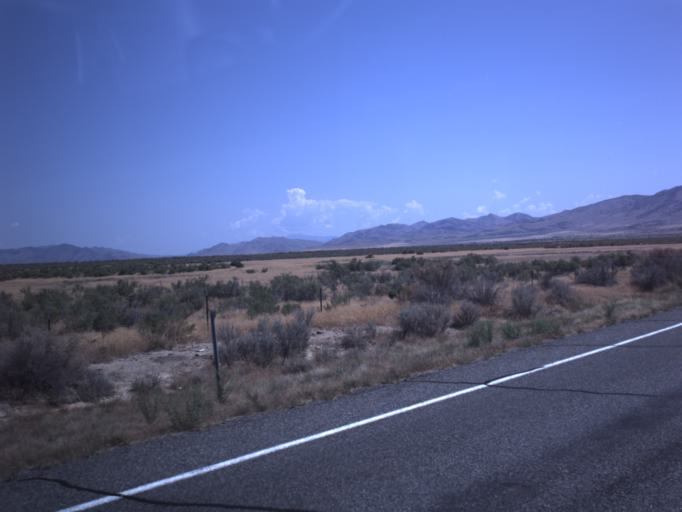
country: US
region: Utah
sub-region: Millard County
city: Delta
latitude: 39.3537
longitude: -112.4496
